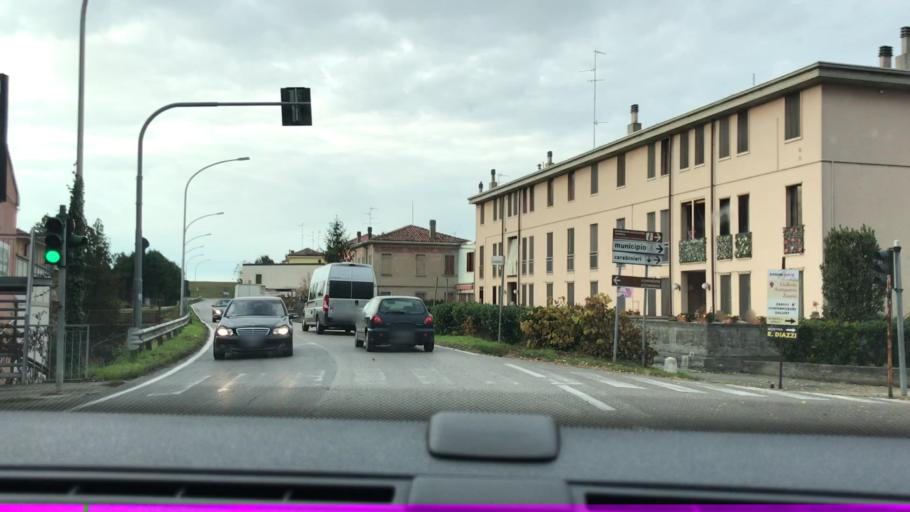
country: IT
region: Lombardy
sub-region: Provincia di Mantova
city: San Benedetto Po
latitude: 45.0391
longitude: 10.9282
